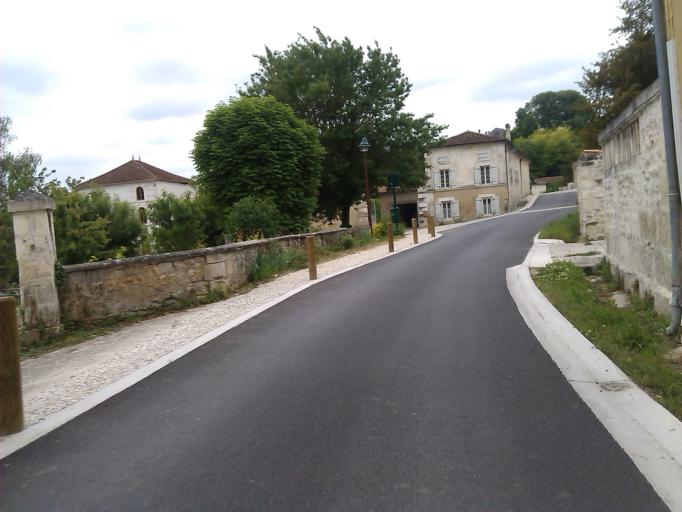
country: FR
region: Poitou-Charentes
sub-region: Departement de la Charente
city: Chateauneuf-sur-Charente
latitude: 45.6258
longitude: -0.0257
